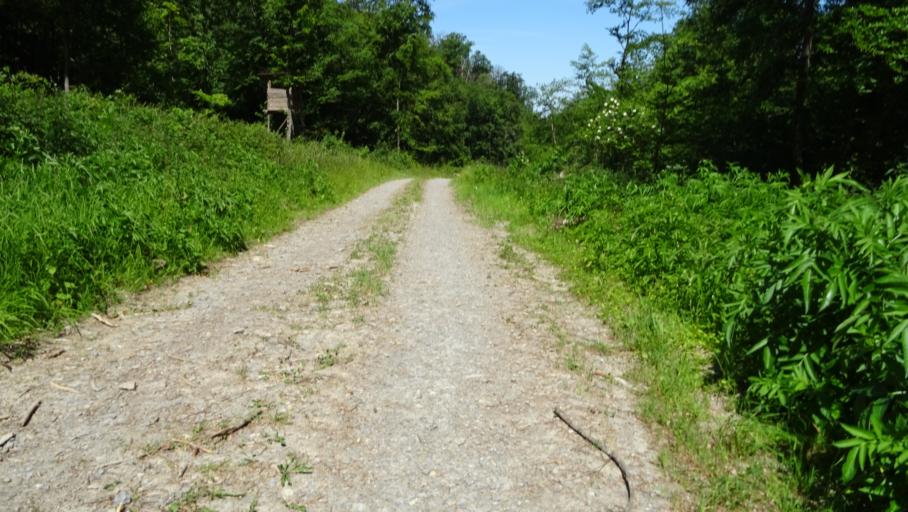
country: DE
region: Baden-Wuerttemberg
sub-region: Karlsruhe Region
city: Obrigheim
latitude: 49.3351
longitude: 9.0786
